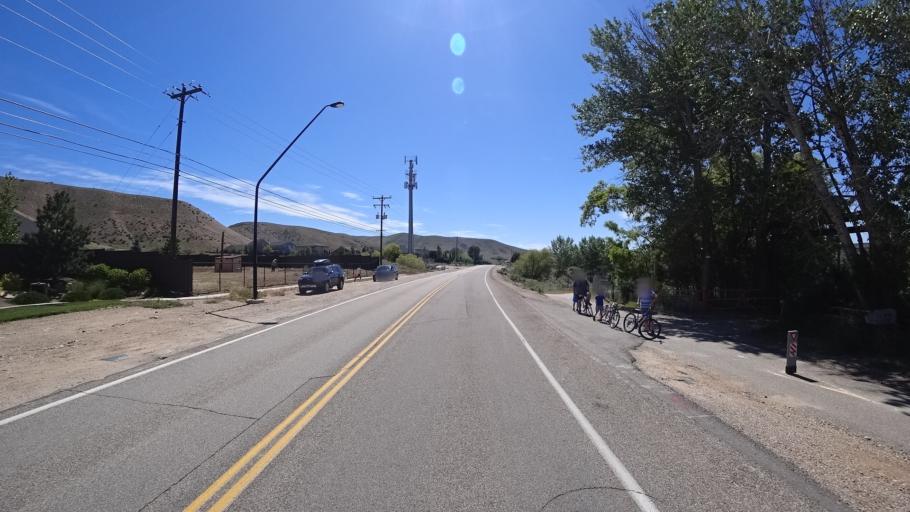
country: US
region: Idaho
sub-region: Ada County
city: Boise
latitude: 43.5621
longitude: -116.1056
